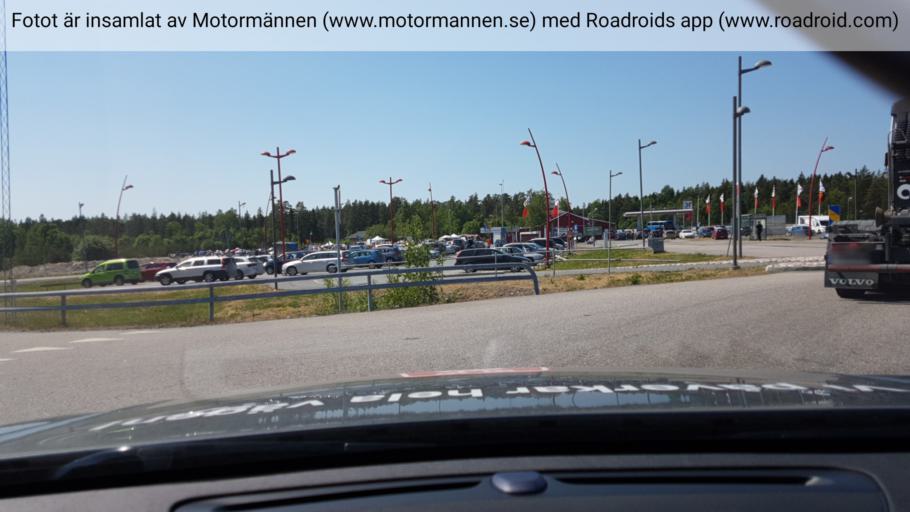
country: SE
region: Stockholm
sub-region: Norrtalje Kommun
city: Rimbo
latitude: 59.6350
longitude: 18.3335
